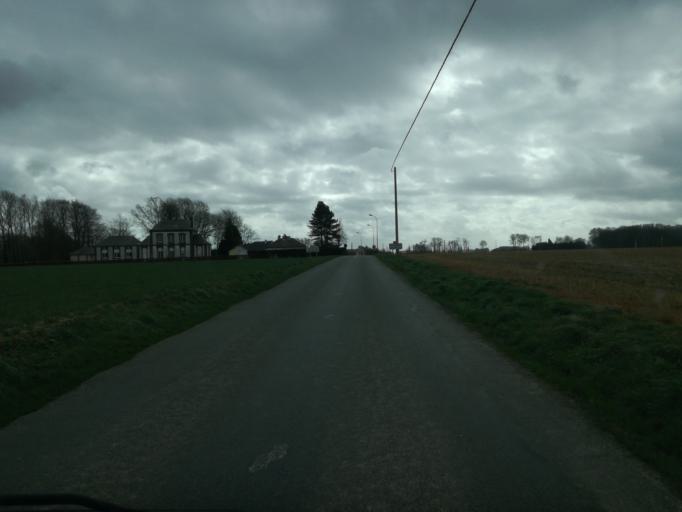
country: FR
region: Haute-Normandie
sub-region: Departement de la Seine-Maritime
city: Yebleron
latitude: 49.6688
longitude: 0.4972
